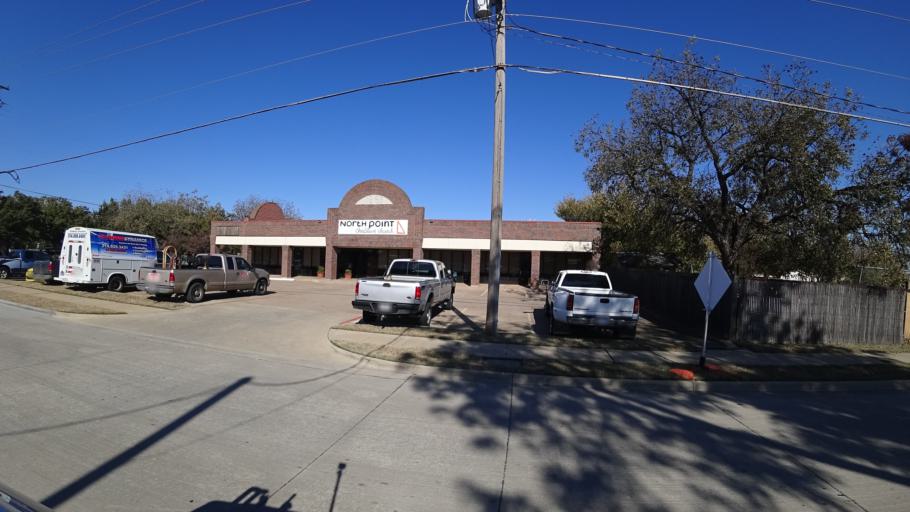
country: US
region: Texas
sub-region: Denton County
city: Lewisville
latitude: 33.0493
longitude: -96.9937
